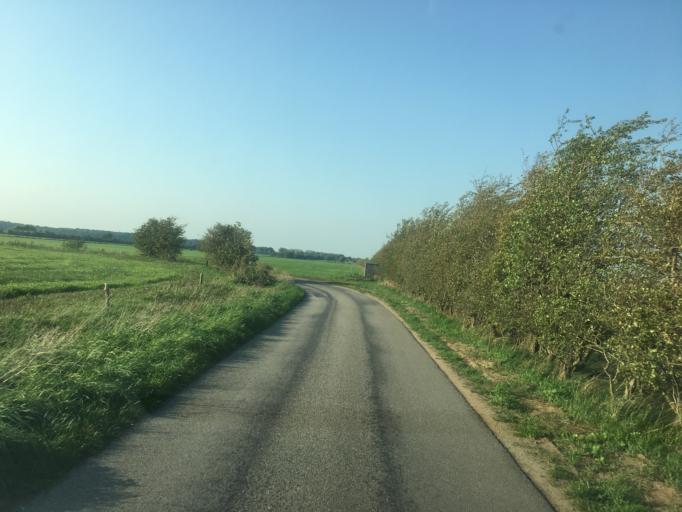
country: DE
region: Schleswig-Holstein
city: Ladelund
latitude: 54.9231
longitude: 9.0349
